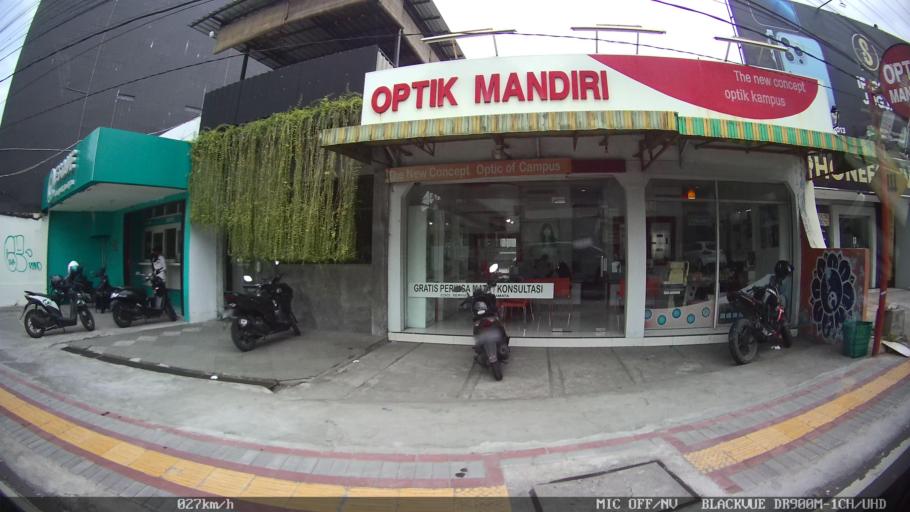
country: ID
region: Daerah Istimewa Yogyakarta
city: Yogyakarta
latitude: -7.7877
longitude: 110.3946
